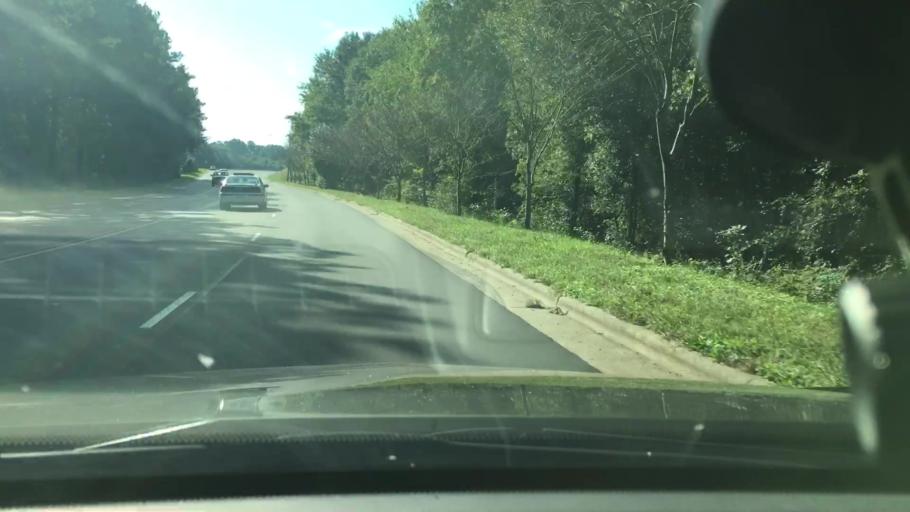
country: US
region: North Carolina
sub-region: Stanly County
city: Albemarle
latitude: 35.3439
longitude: -80.2030
